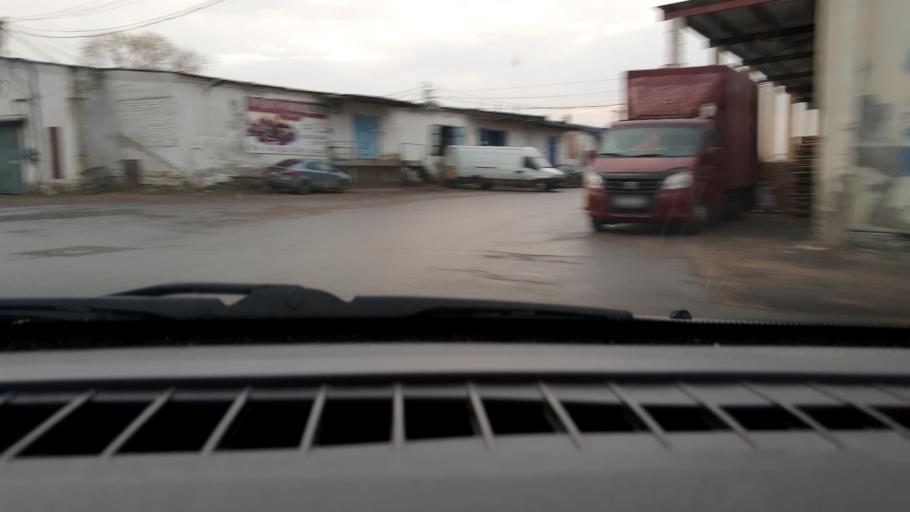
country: RU
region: Nizjnij Novgorod
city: Gorbatovka
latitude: 56.3101
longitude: 43.8638
